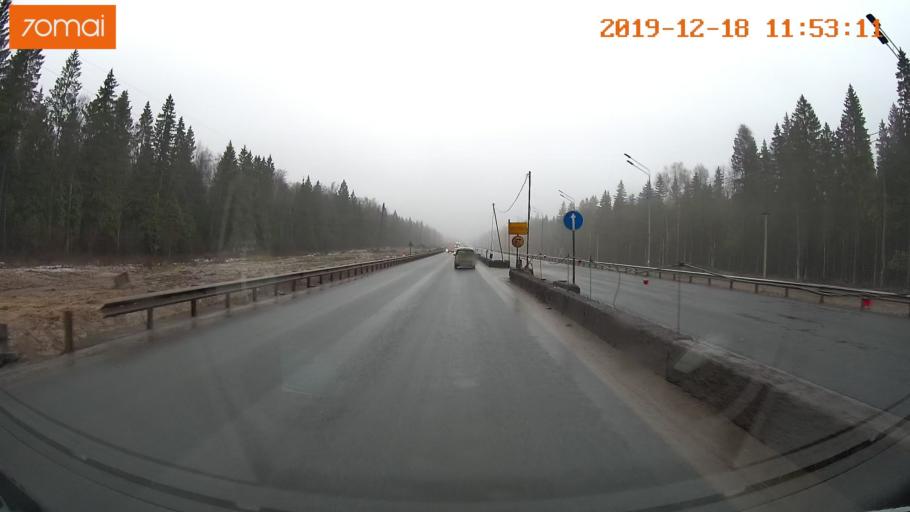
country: RU
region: Moskovskaya
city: Yershovo
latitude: 55.8018
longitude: 36.9205
